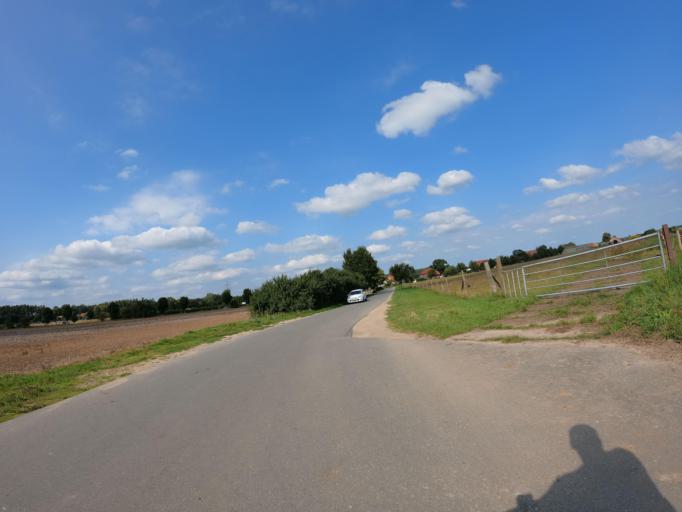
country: DE
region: Mecklenburg-Vorpommern
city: Malchow
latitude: 53.5158
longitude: 12.4413
